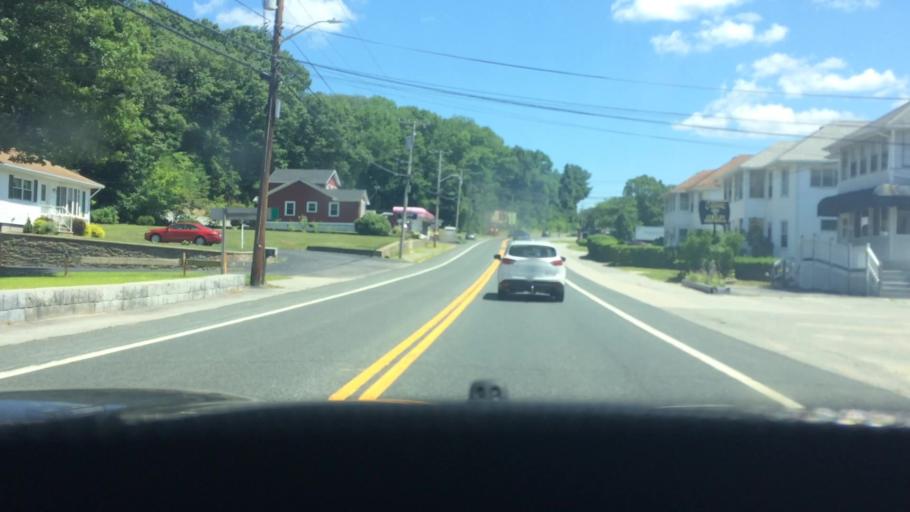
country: US
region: Massachusetts
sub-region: Worcester County
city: Blackstone
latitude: 41.9994
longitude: -71.5505
